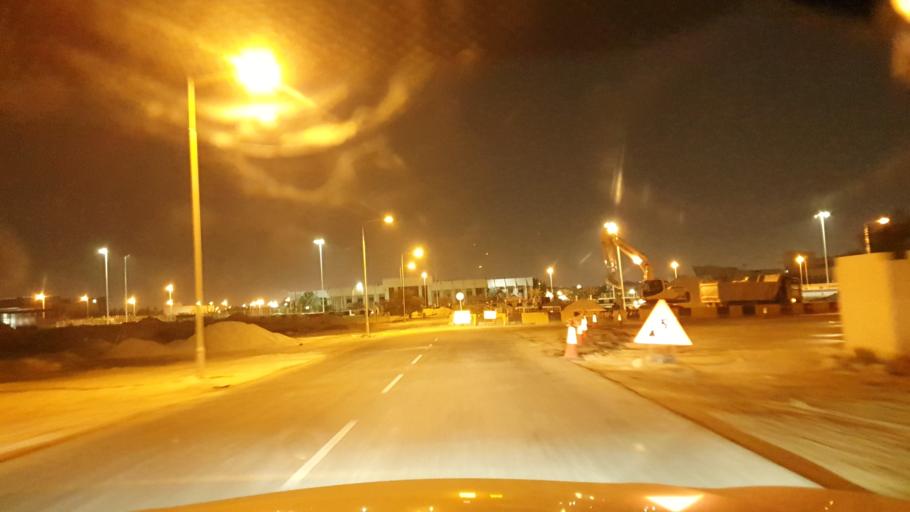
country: BH
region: Northern
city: Madinat `Isa
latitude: 26.1560
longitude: 50.5486
